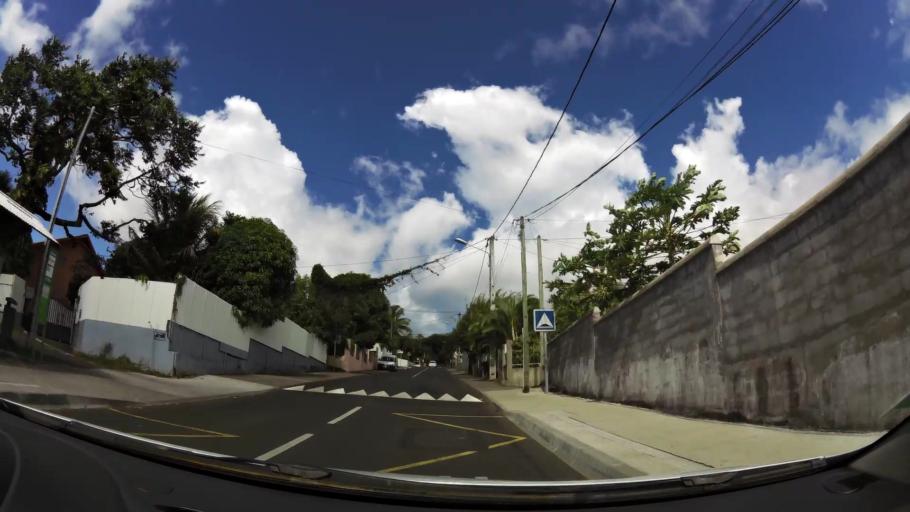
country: RE
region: Reunion
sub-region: Reunion
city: Saint-Denis
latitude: -20.9271
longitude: 55.4934
